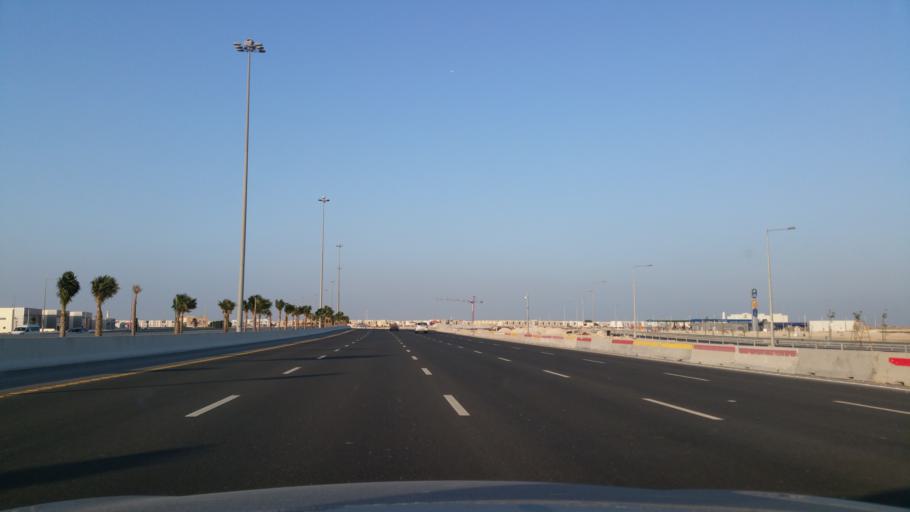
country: QA
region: Al Khawr
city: Al Khawr
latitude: 25.6546
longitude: 51.4986
